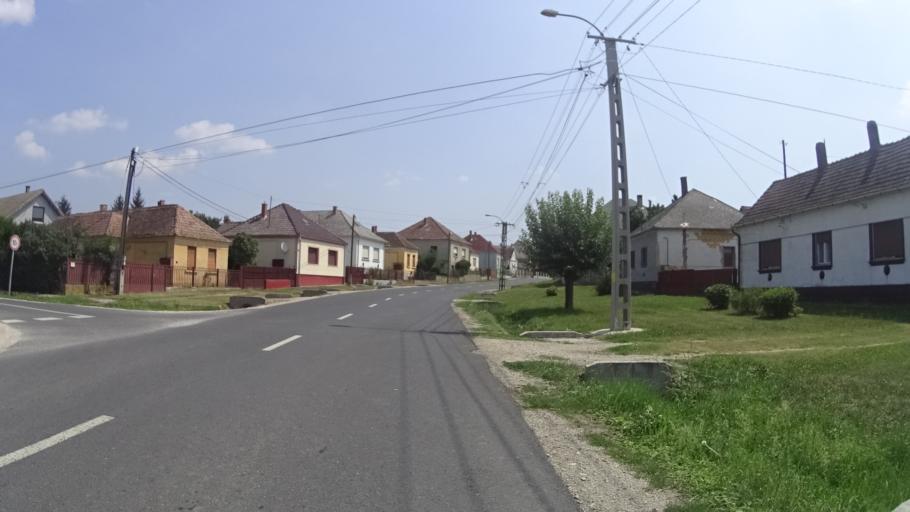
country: HU
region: Zala
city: Letenye
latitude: 46.4258
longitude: 16.7250
